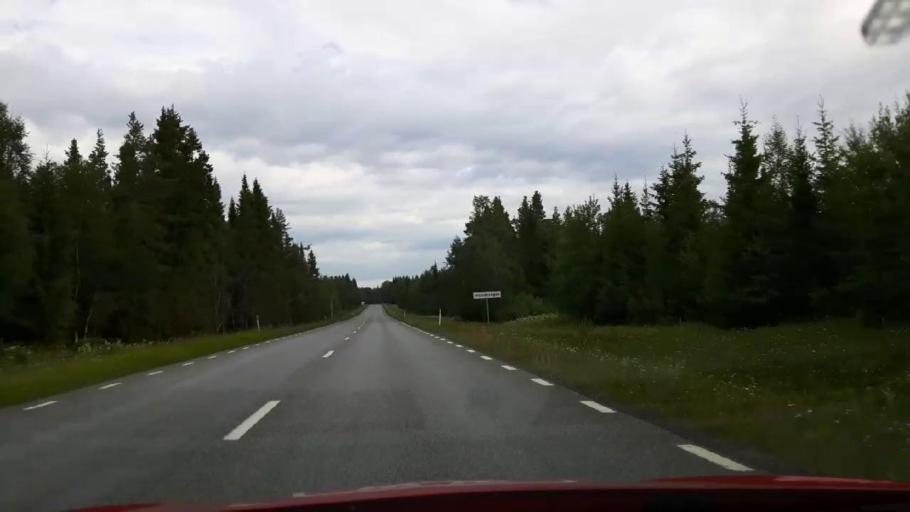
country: SE
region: Jaemtland
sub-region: Stroemsunds Kommun
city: Stroemsund
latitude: 63.5489
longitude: 15.3722
